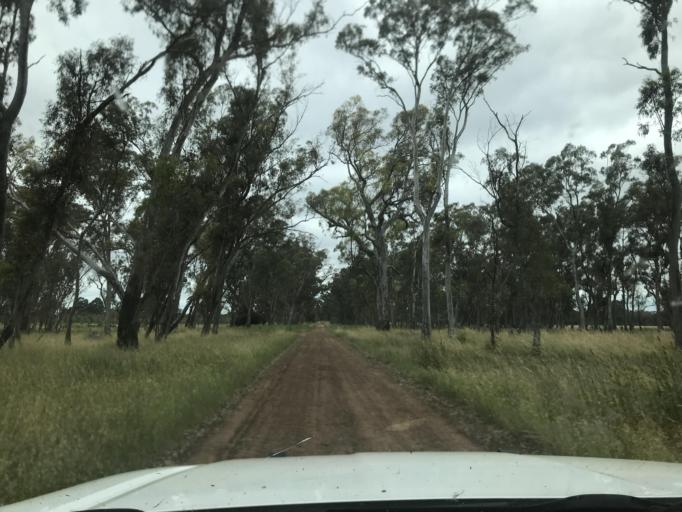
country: AU
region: South Australia
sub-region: Wattle Range
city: Penola
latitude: -37.2441
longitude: 141.1210
